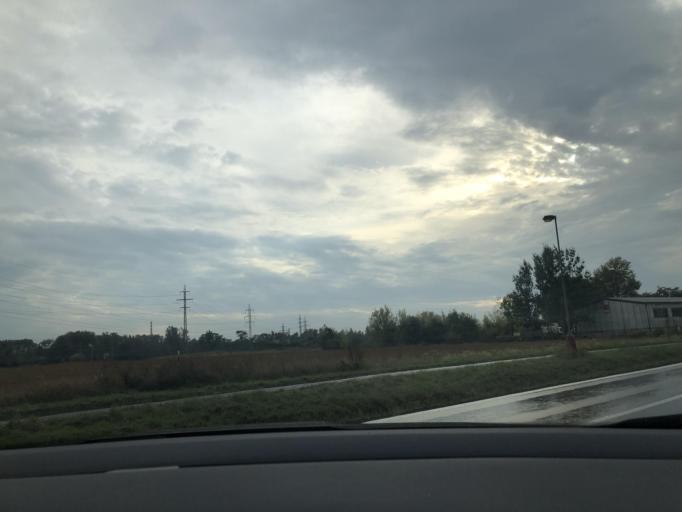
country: CZ
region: Central Bohemia
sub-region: Okres Kolin
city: Kolin
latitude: 50.0329
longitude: 15.2251
